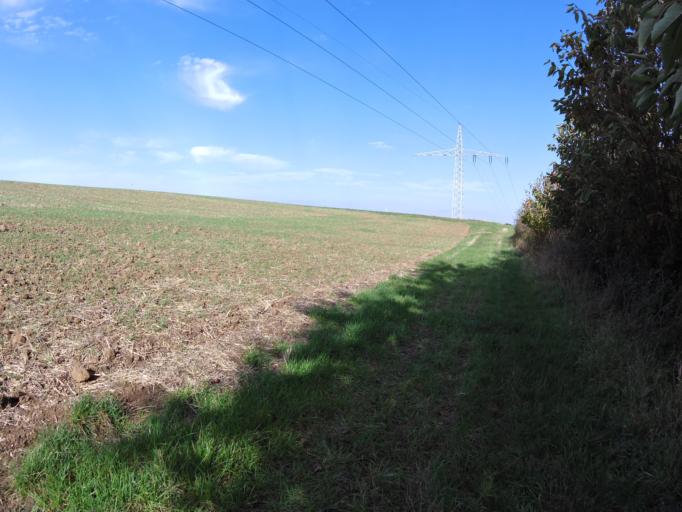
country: DE
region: Bavaria
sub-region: Regierungsbezirk Unterfranken
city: Theilheim
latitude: 49.7524
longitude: 10.0549
